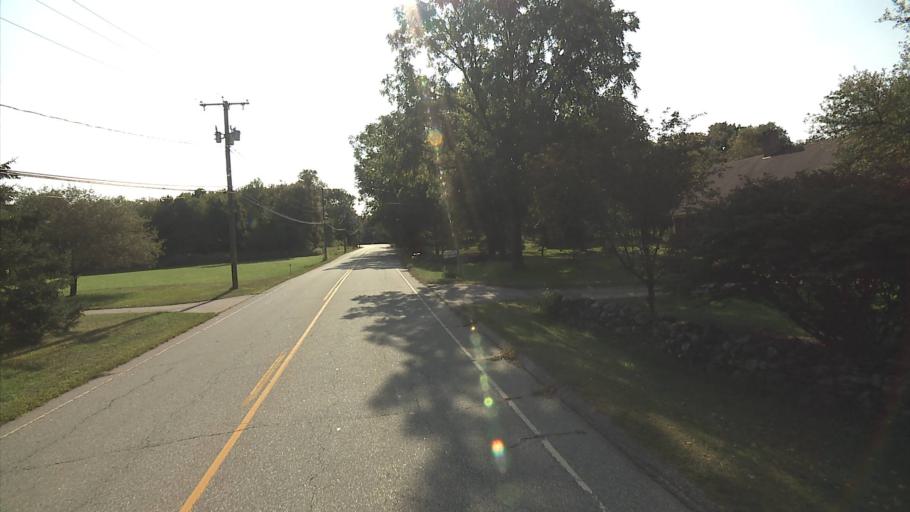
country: US
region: Connecticut
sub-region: Windham County
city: Willimantic
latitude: 41.6468
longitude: -72.2316
